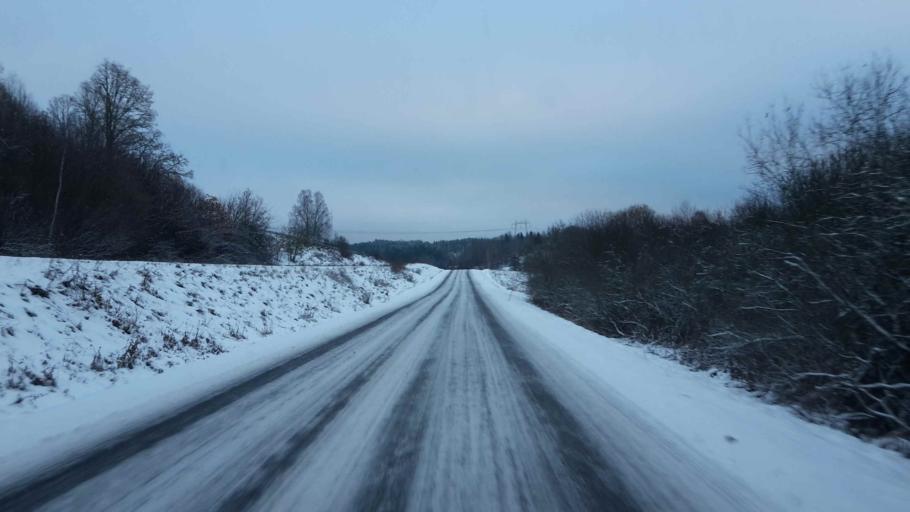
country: SE
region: OEstergoetland
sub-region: Atvidabergs Kommun
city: Atvidaberg
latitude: 58.1494
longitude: 16.1751
